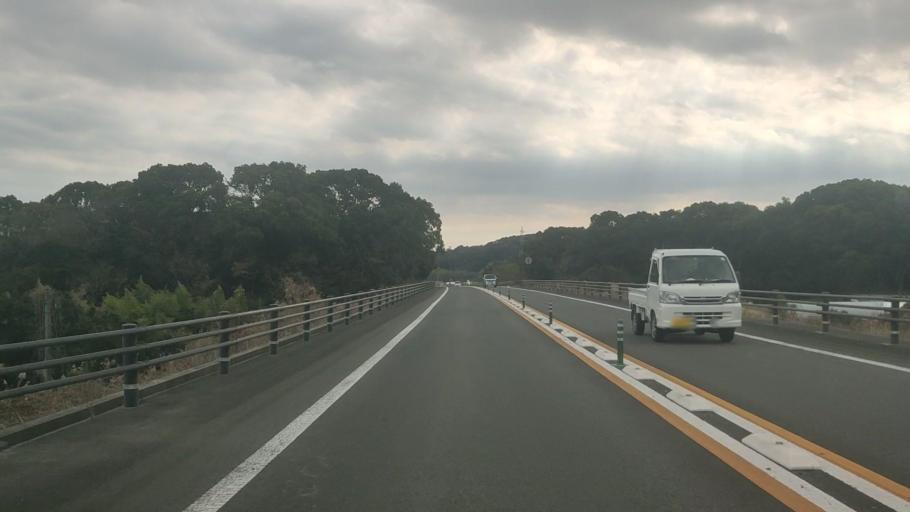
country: JP
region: Nagasaki
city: Shimabara
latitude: 32.7663
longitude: 130.3600
